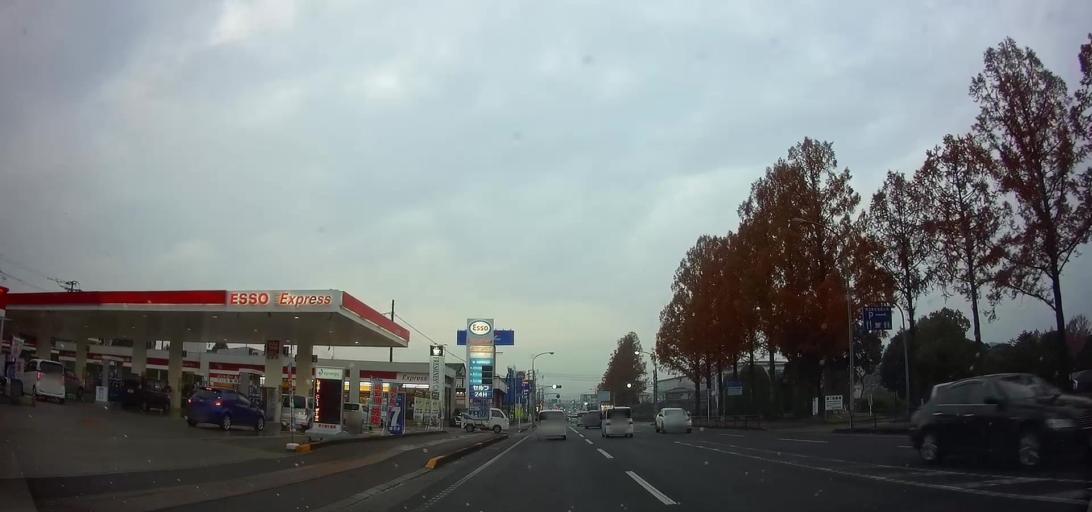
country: JP
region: Nagasaki
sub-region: Isahaya-shi
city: Isahaya
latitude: 32.8376
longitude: 130.0374
